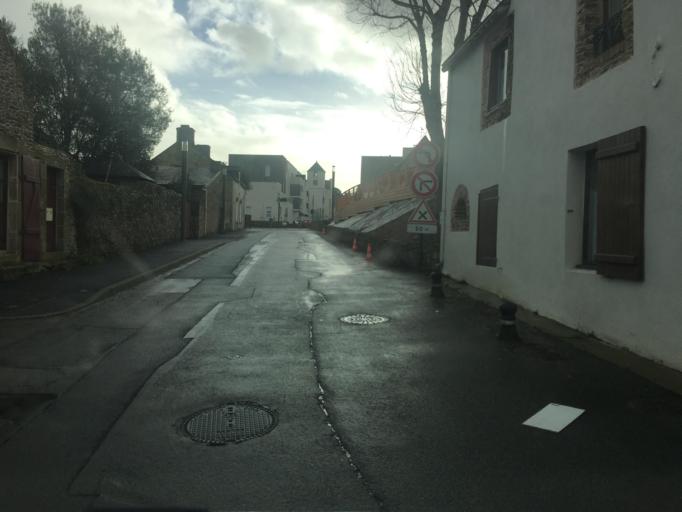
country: FR
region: Brittany
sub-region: Departement du Morbihan
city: Sarzeau
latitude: 47.5279
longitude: -2.7722
